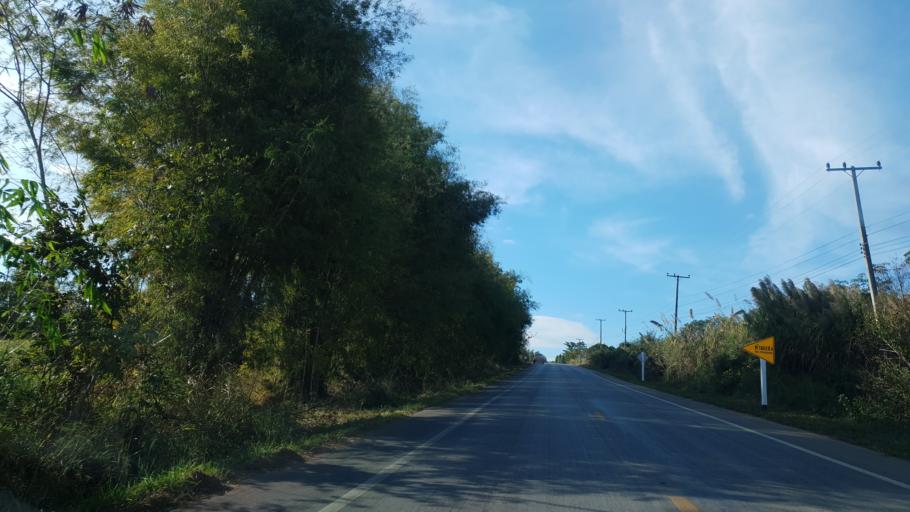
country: TH
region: Loei
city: Phu Ruea
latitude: 17.4415
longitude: 101.5036
